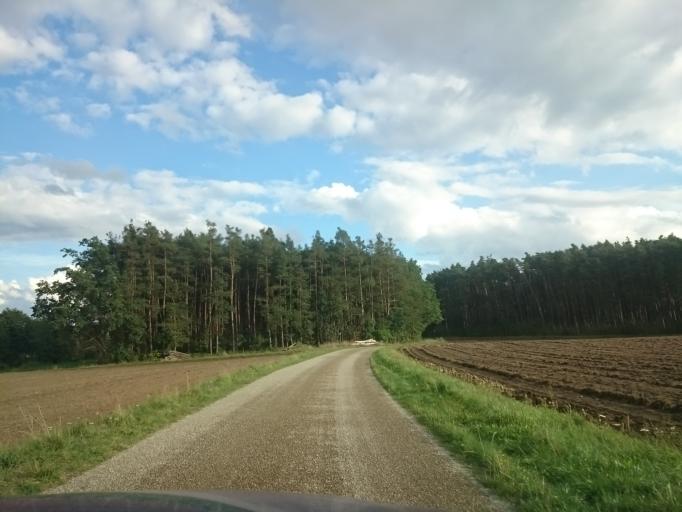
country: DE
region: Bavaria
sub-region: Regierungsbezirk Mittelfranken
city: Hilpoltstein
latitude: 49.1549
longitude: 11.1751
